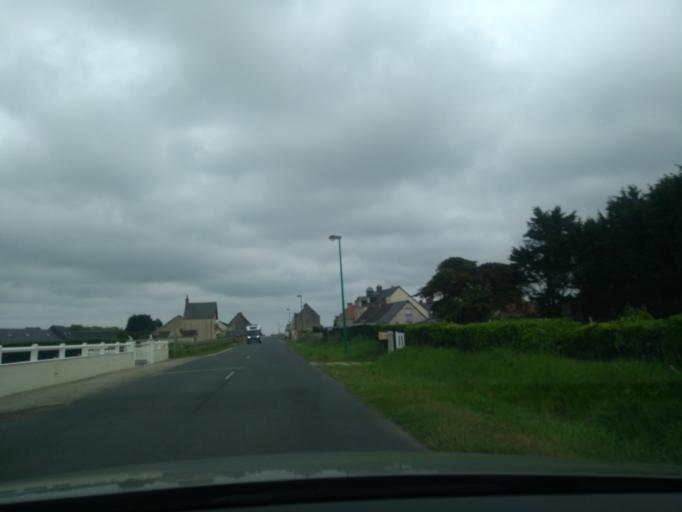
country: FR
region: Lower Normandy
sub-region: Departement de la Manche
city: Sainte-Mere-Eglise
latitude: 49.4716
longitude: -1.2476
